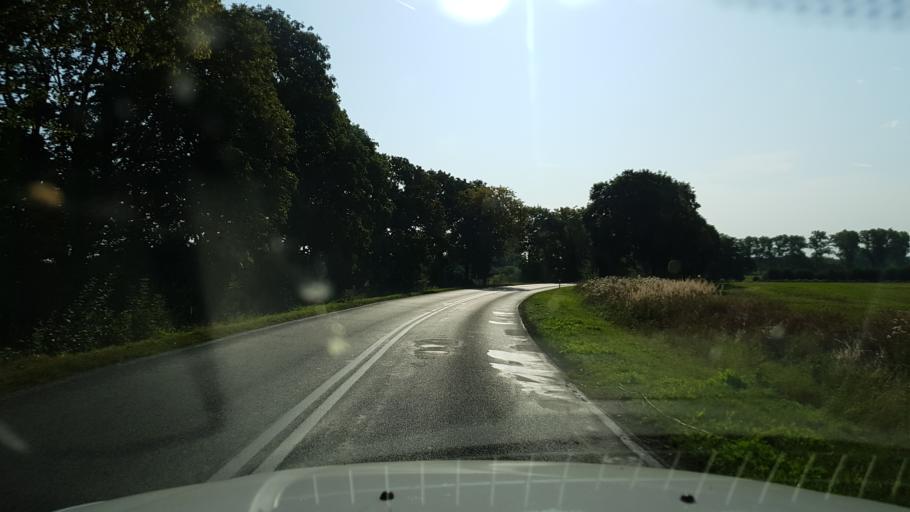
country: PL
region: West Pomeranian Voivodeship
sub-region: Powiat lobeski
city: Resko
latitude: 53.7788
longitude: 15.3608
